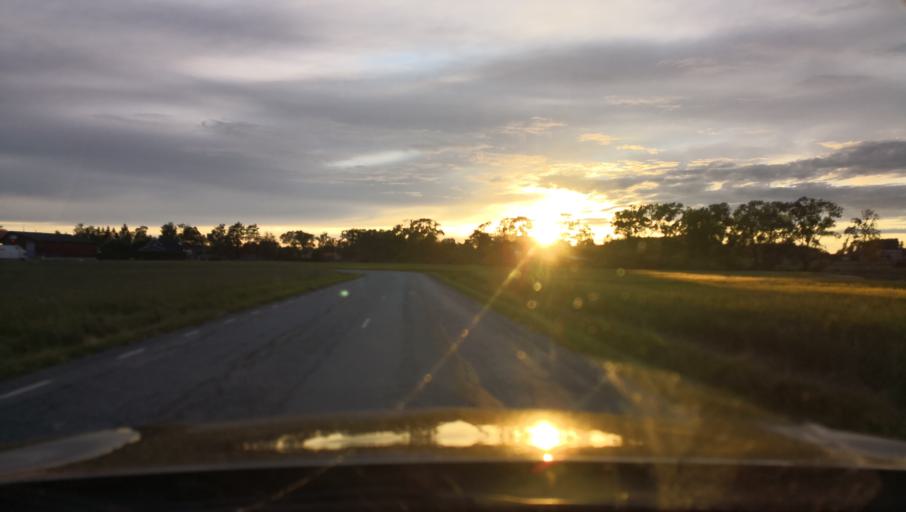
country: SE
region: Uppsala
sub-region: Enkopings Kommun
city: Grillby
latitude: 59.6569
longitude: 17.2514
